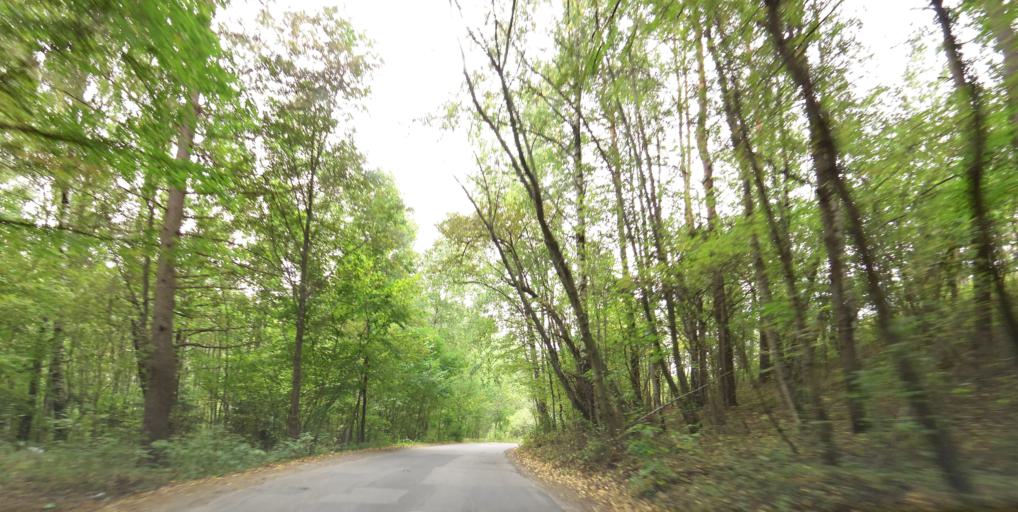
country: LT
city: Grigiskes
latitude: 54.7593
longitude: 25.0378
